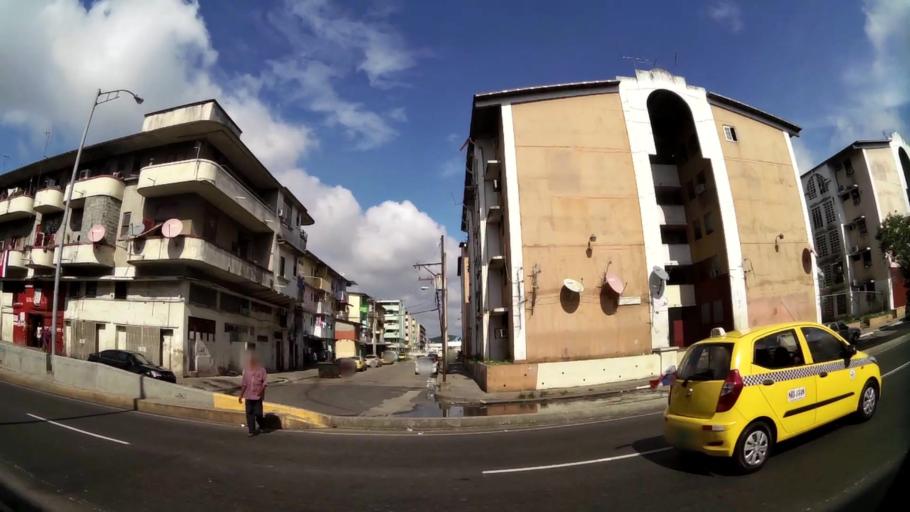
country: PA
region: Panama
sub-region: Distrito de Panama
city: Ancon
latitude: 8.9661
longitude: -79.5433
